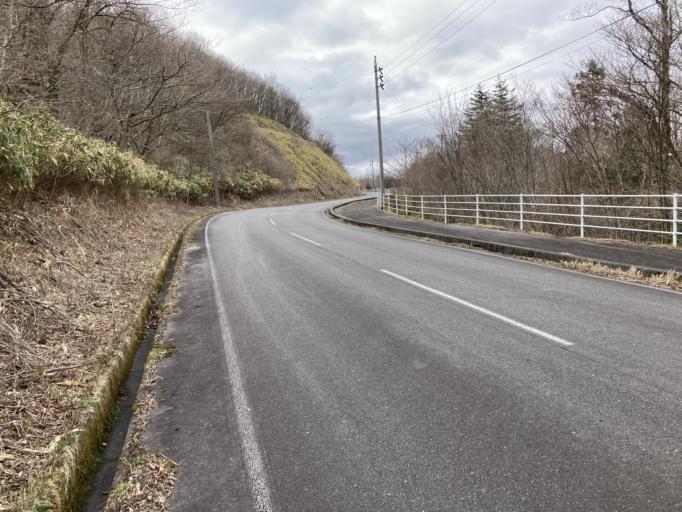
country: JP
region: Gifu
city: Nakatsugawa
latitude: 35.2297
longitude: 137.6580
